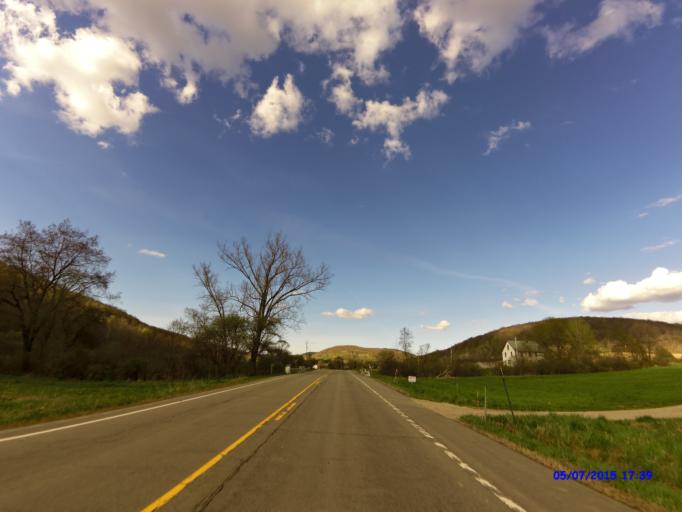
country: US
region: New York
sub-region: Cattaraugus County
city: Franklinville
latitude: 42.2656
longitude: -78.5444
